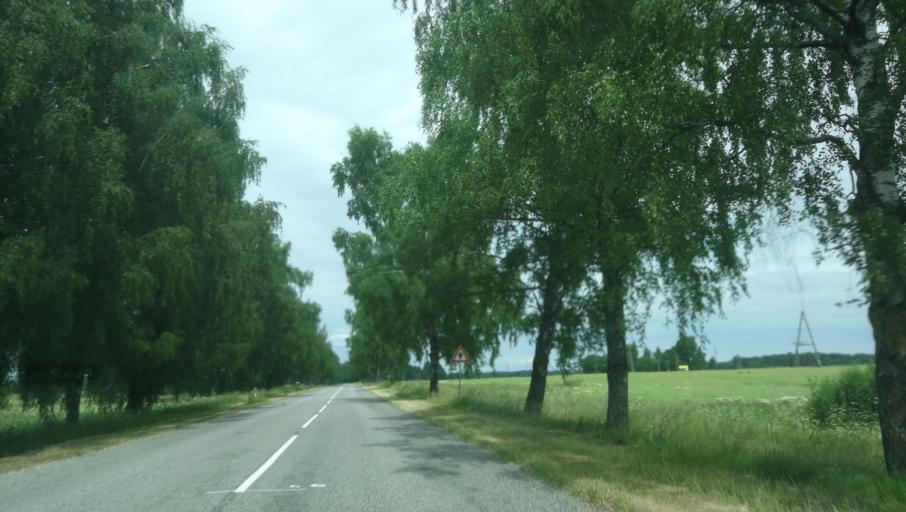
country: LV
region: Valmieras Rajons
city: Valmiera
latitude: 57.6312
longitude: 25.4477
